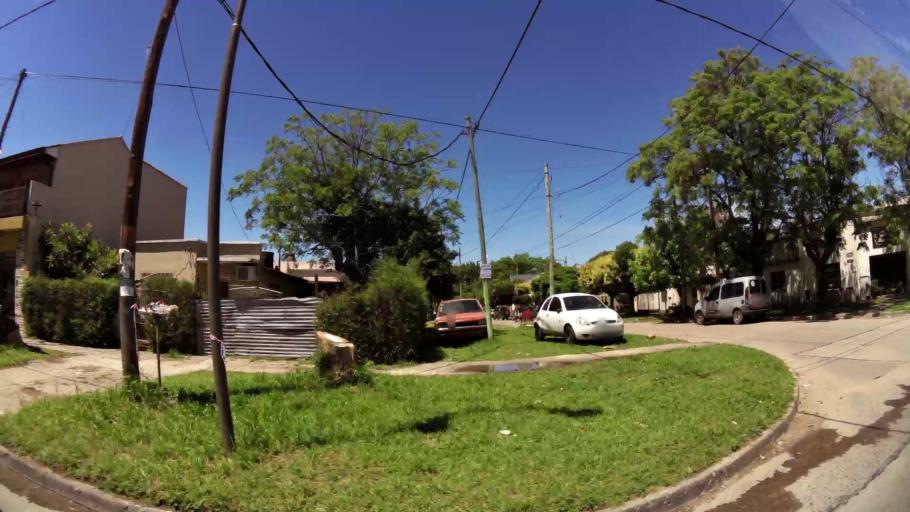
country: AR
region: Buenos Aires
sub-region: Partido de Quilmes
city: Quilmes
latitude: -34.7312
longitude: -58.2856
